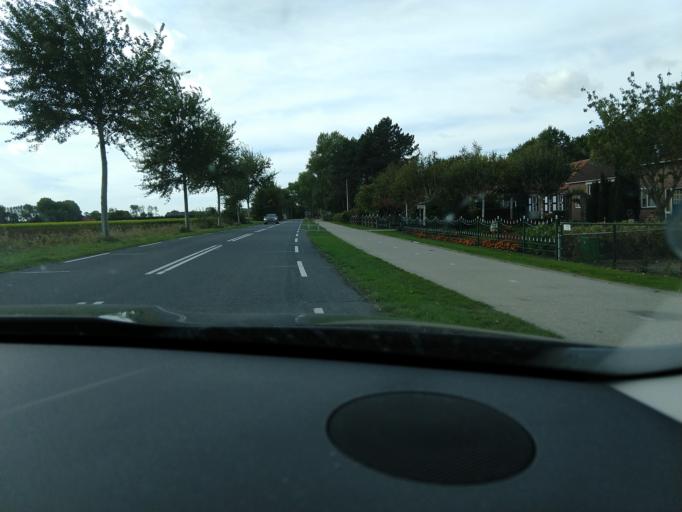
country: NL
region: Zeeland
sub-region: Gemeente Vlissingen
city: Vlissingen
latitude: 51.5150
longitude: 3.5203
